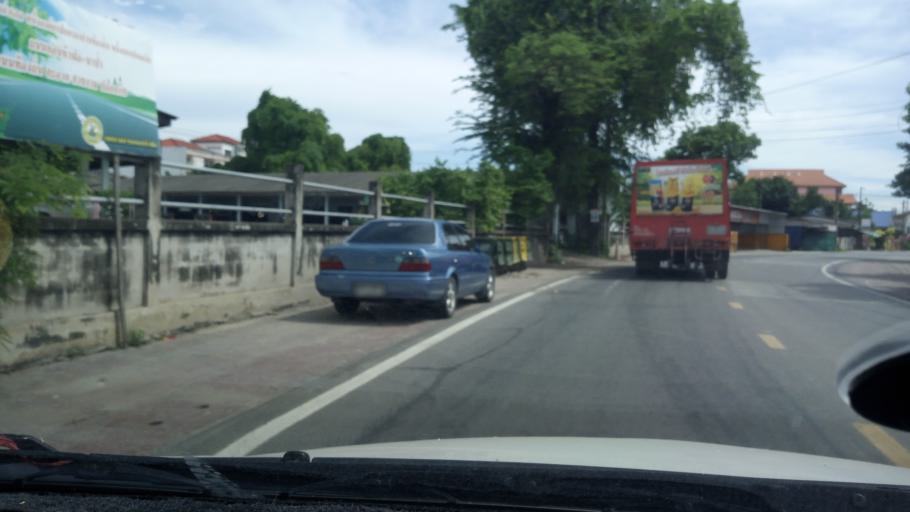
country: TH
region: Chon Buri
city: Phan Thong
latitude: 13.4260
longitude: 101.0395
